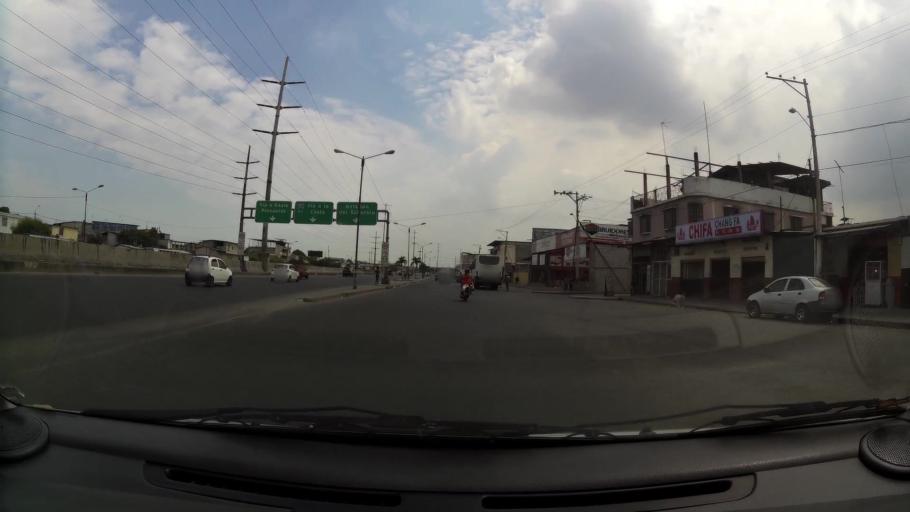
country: EC
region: Guayas
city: Guayaquil
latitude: -2.2395
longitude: -79.9157
